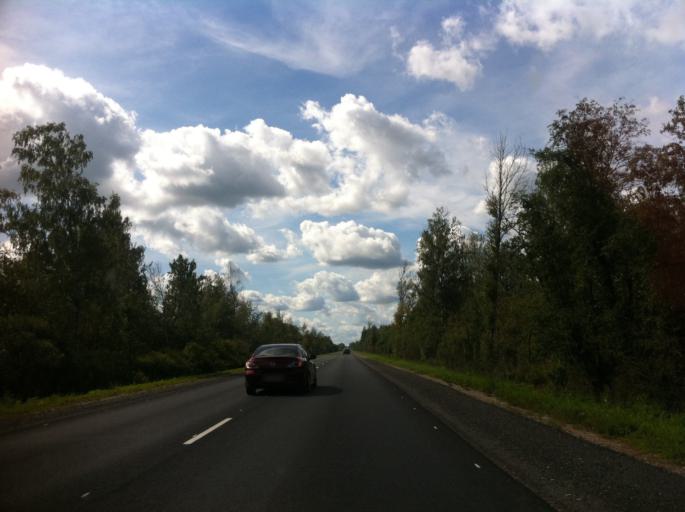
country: RU
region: Pskov
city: Izborsk
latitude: 57.7456
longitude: 28.0308
